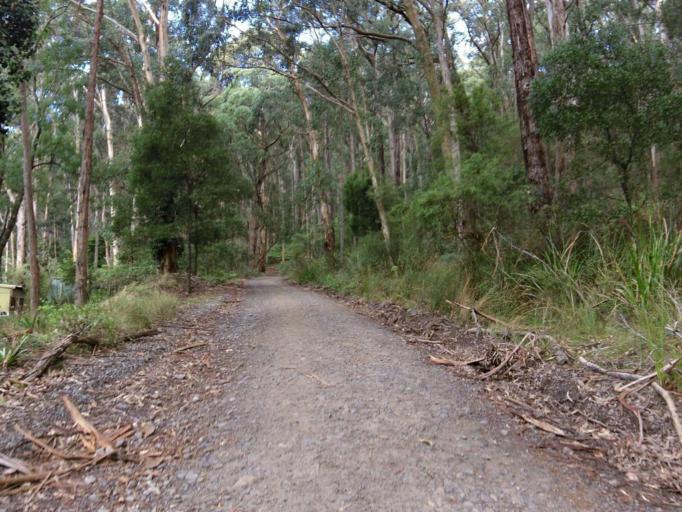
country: AU
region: Victoria
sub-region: Yarra Ranges
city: Ferny Creek
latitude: -37.8604
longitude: 145.3407
